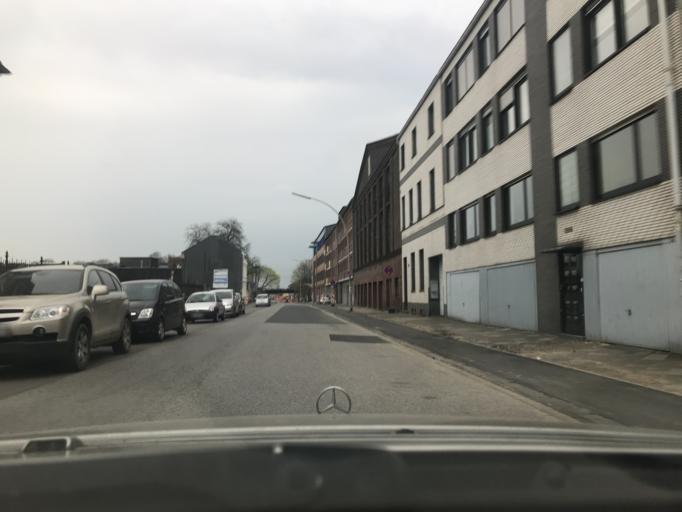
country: DE
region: North Rhine-Westphalia
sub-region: Regierungsbezirk Dusseldorf
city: Monchengladbach
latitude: 51.2051
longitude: 6.4528
